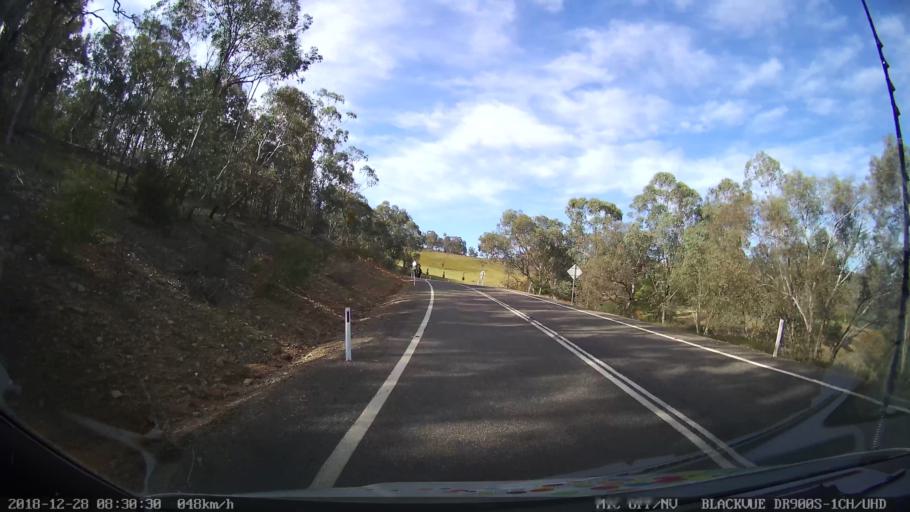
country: AU
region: New South Wales
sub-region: Blayney
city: Blayney
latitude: -33.9562
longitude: 149.3245
